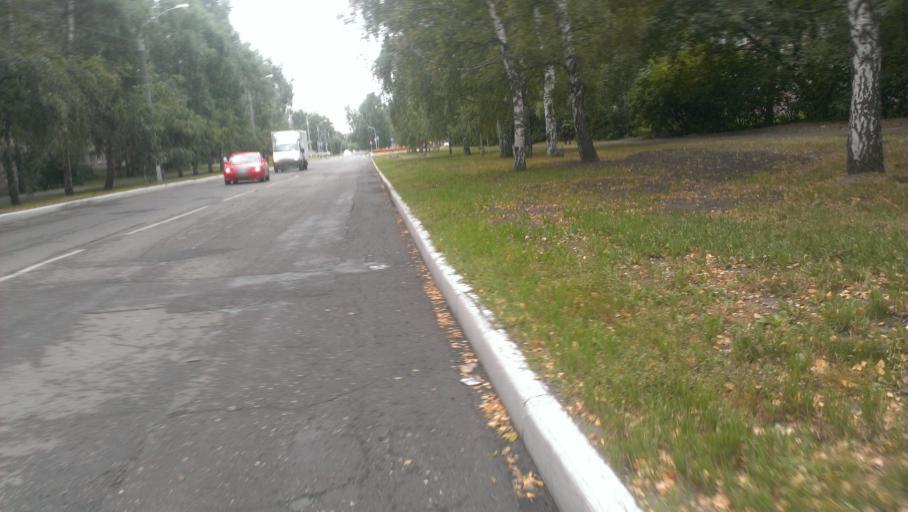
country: RU
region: Altai Krai
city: Novosilikatnyy
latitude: 53.3690
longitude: 83.6690
